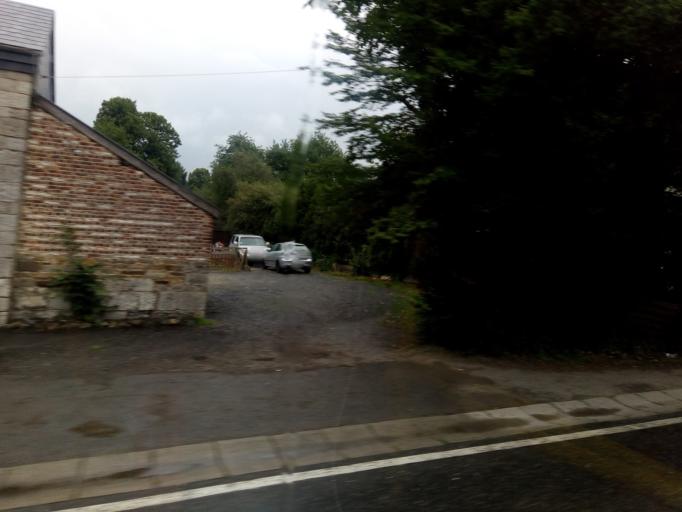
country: BE
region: Wallonia
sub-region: Province du Luxembourg
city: Hotton
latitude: 50.2574
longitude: 5.4738
